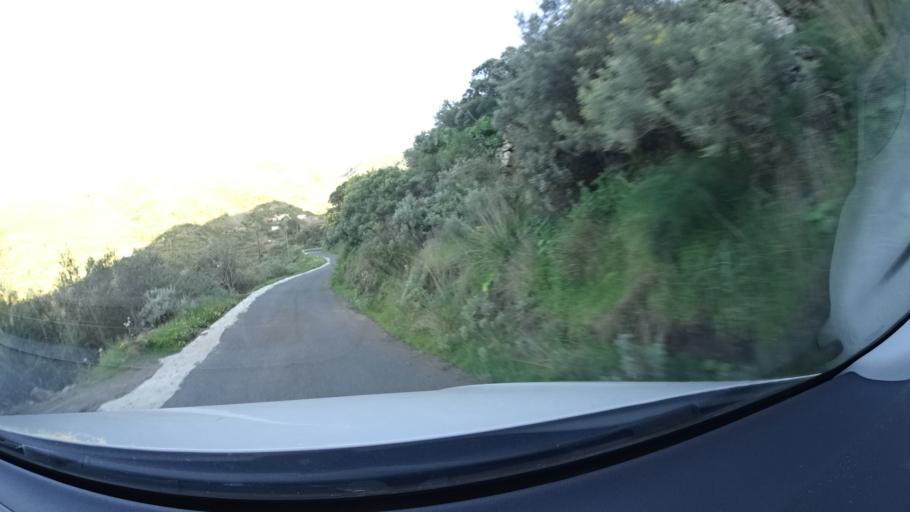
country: ES
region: Canary Islands
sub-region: Provincia de Las Palmas
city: Artenara
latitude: 28.0354
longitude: -15.6494
